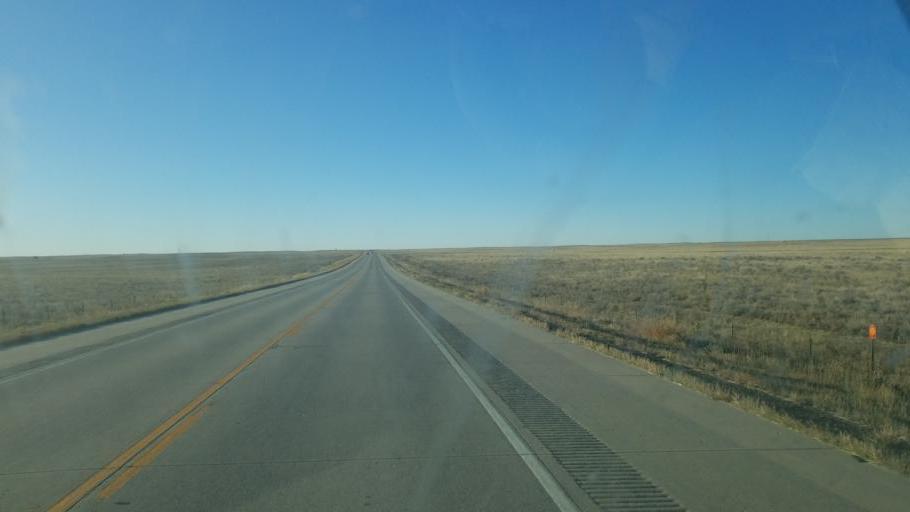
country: US
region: Colorado
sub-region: Kiowa County
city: Eads
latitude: 38.5767
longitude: -102.7862
